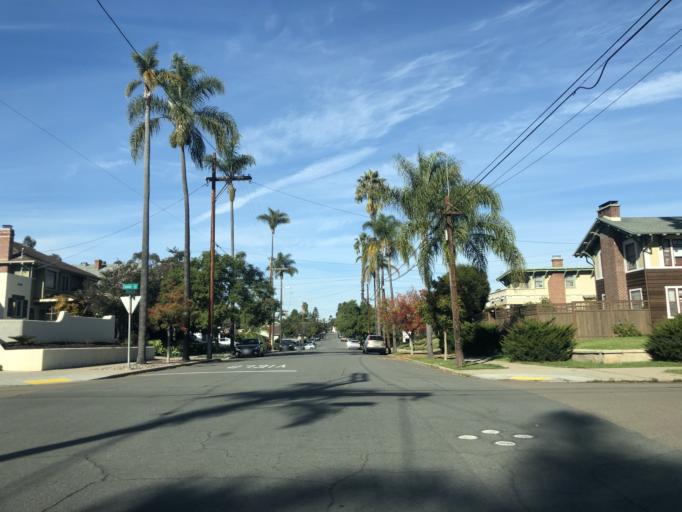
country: US
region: California
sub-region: San Diego County
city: San Diego
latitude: 32.7223
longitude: -117.1330
